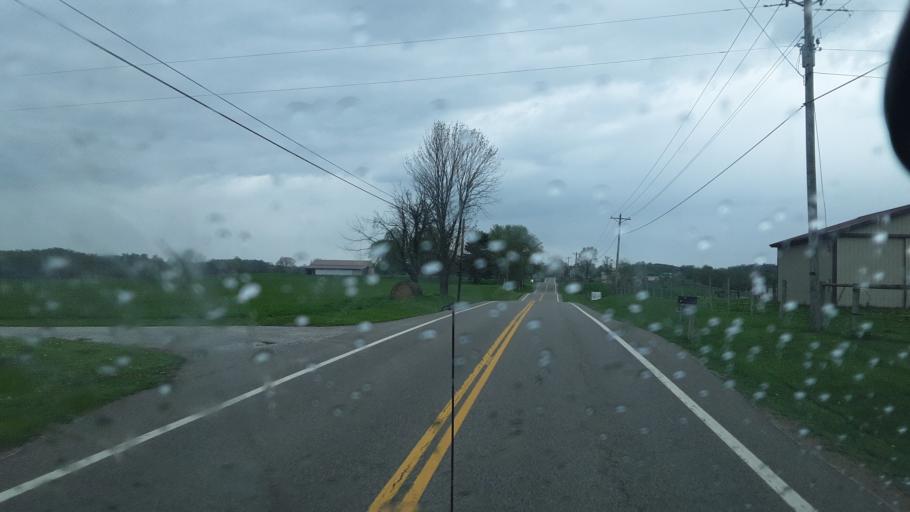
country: US
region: Ohio
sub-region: Muskingum County
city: New Concord
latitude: 39.9231
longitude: -81.6786
